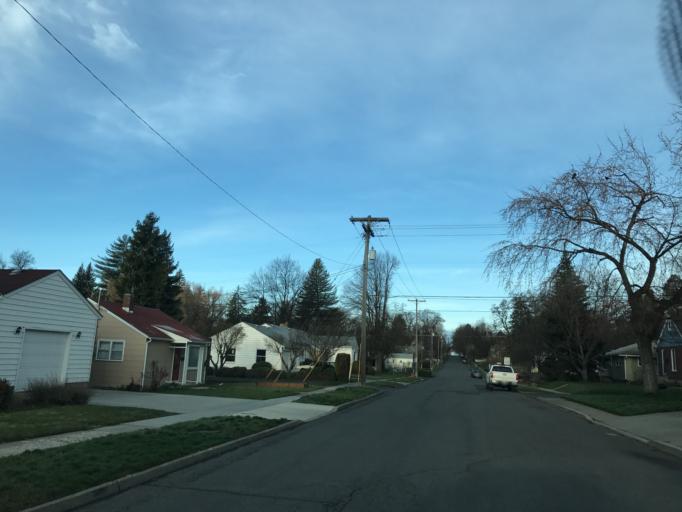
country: US
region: Idaho
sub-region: Latah County
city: Moscow
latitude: 46.7347
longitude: -116.9887
